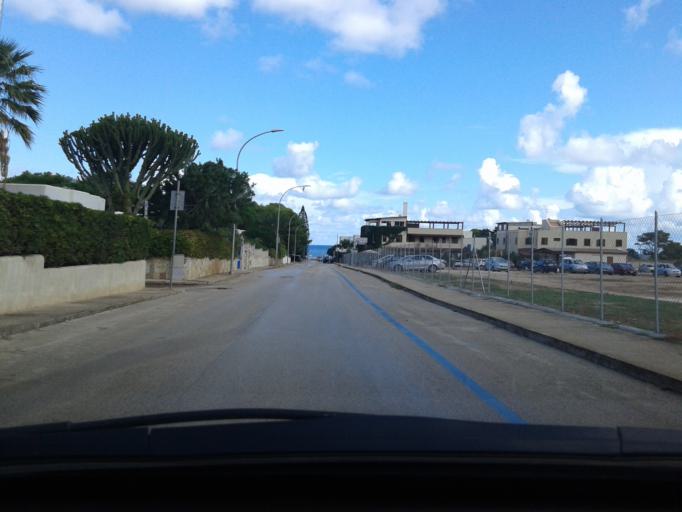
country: IT
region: Sicily
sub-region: Trapani
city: San Vito Lo Capo
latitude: 38.1726
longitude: 12.7423
